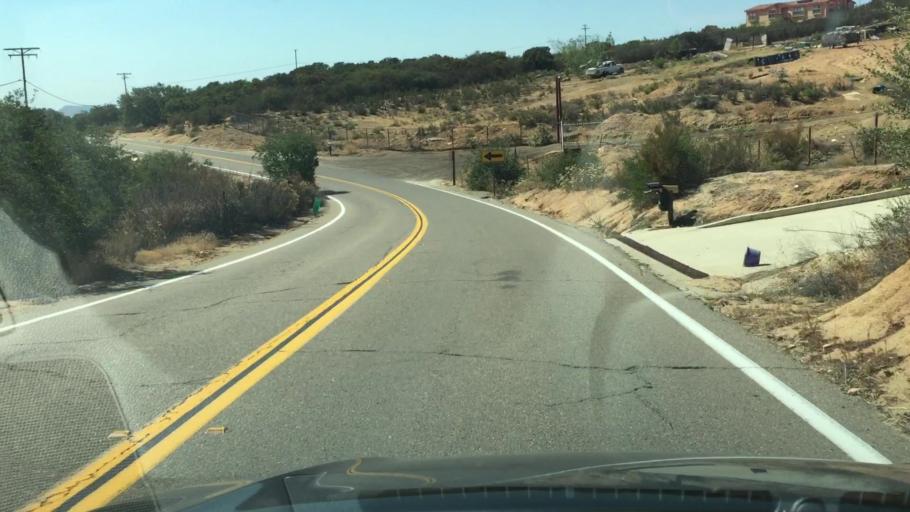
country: US
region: California
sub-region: San Diego County
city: Alpine
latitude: 32.7535
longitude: -116.7630
